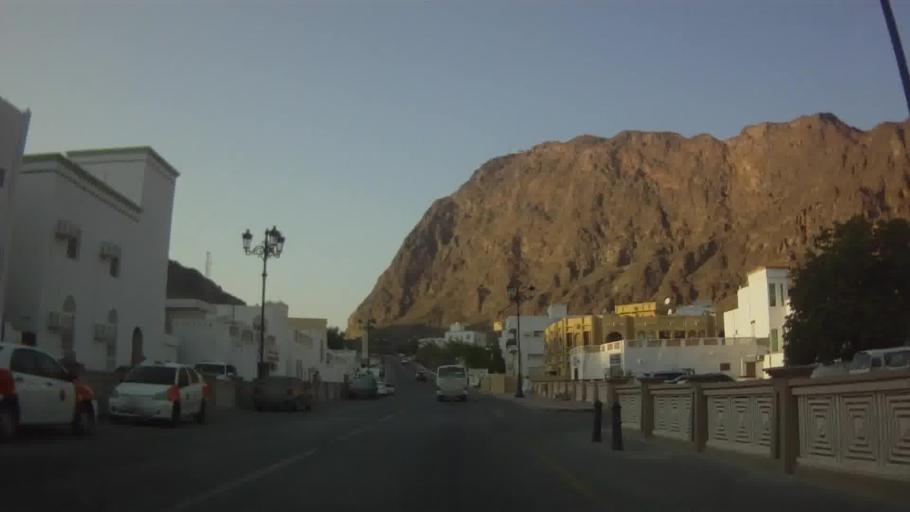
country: OM
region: Muhafazat Masqat
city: Muscat
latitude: 23.6041
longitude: 58.5975
